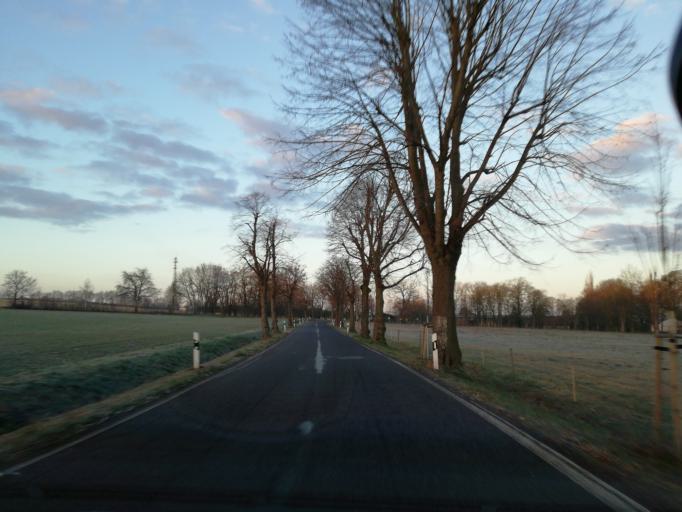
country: DE
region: Brandenburg
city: Calau
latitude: 51.7353
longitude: 13.9176
